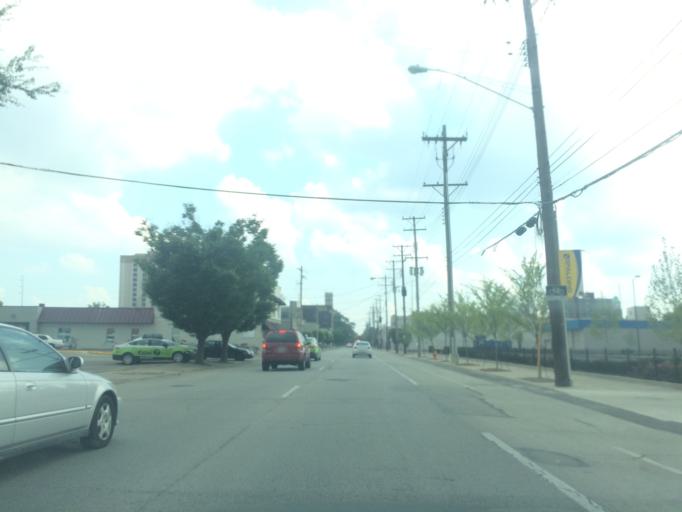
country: US
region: Kentucky
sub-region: Jefferson County
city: Louisville
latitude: 38.2412
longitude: -85.7576
